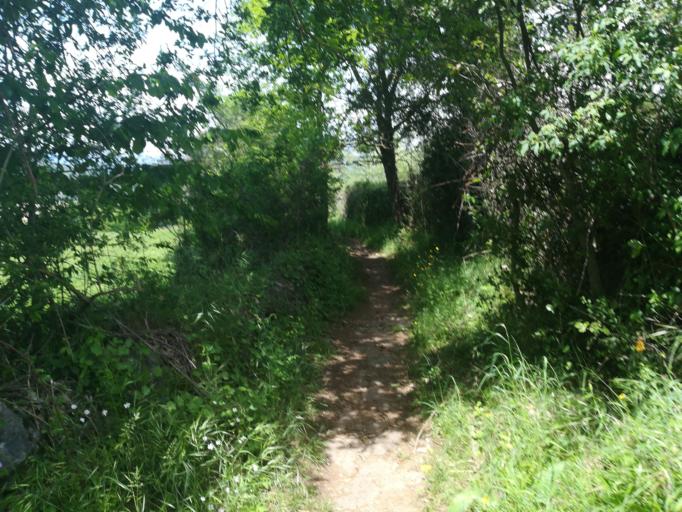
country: ES
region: Catalonia
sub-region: Provincia de Girona
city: Sant Cristofol de les Fonts
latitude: 42.1768
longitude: 2.4993
